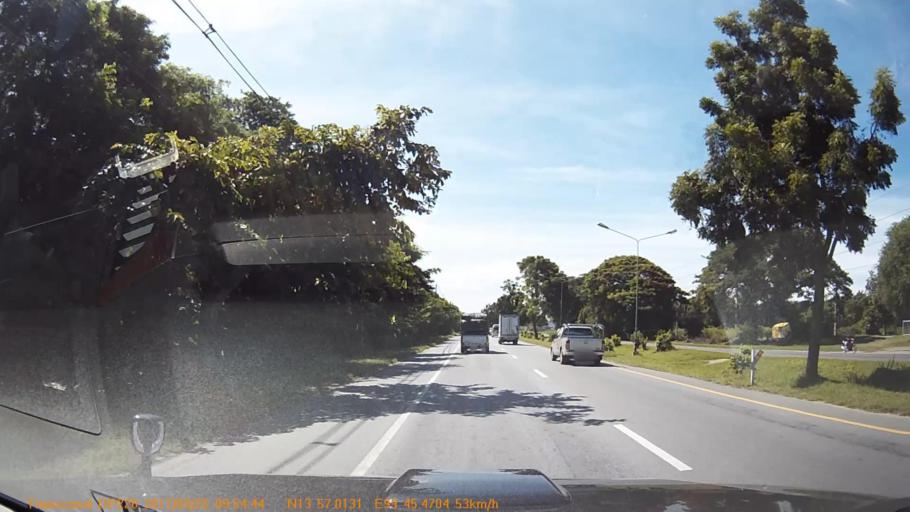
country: TH
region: Kanchanaburi
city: Tha Maka
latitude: 13.9499
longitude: 99.7580
